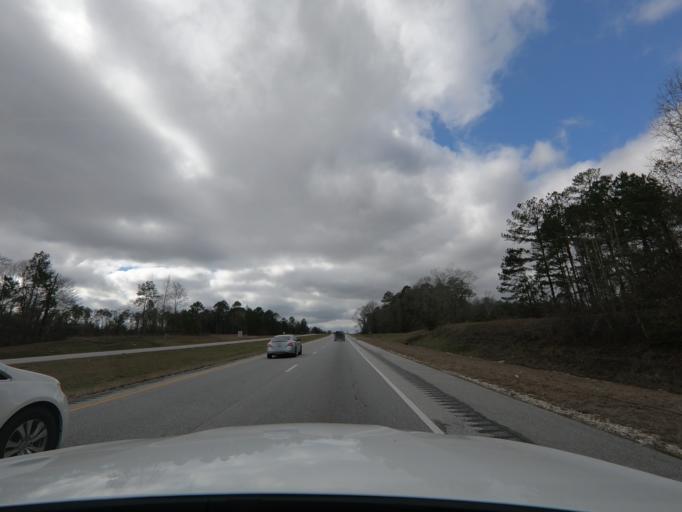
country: US
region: Alabama
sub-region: Russell County
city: Ladonia
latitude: 32.3481
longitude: -85.1246
